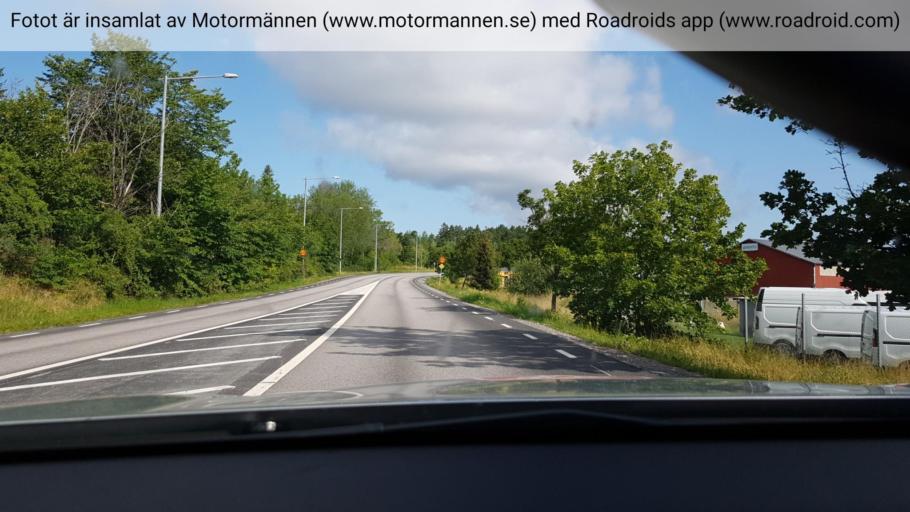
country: SE
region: Uppsala
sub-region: Knivsta Kommun
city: Knivsta
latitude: 59.7216
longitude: 17.7759
